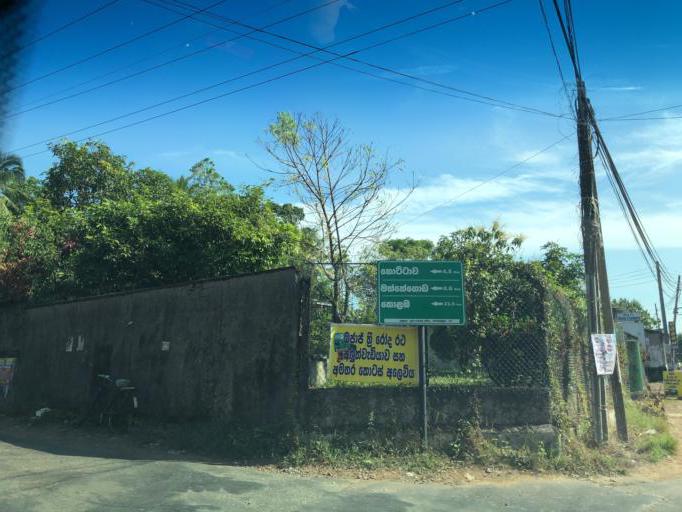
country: LK
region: Western
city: Homagama
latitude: 6.8067
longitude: 79.9794
